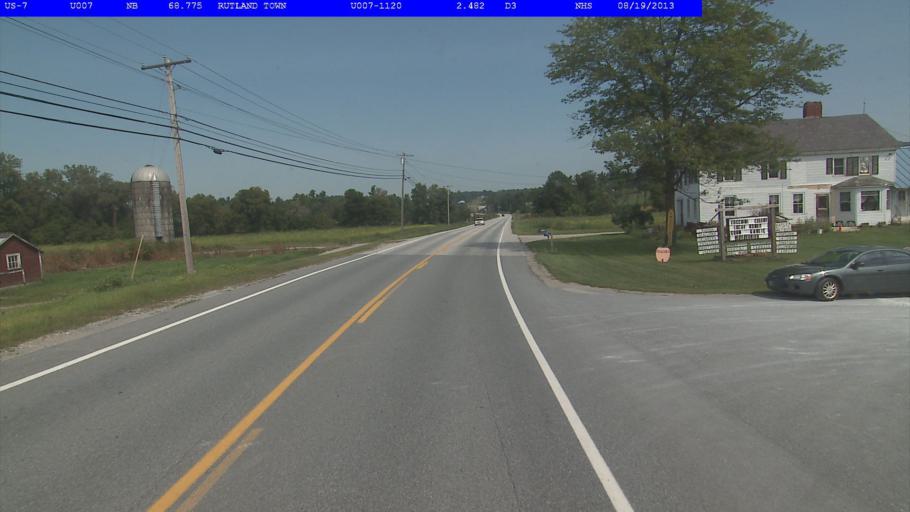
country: US
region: Vermont
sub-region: Rutland County
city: Rutland
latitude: 43.6465
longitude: -72.9854
